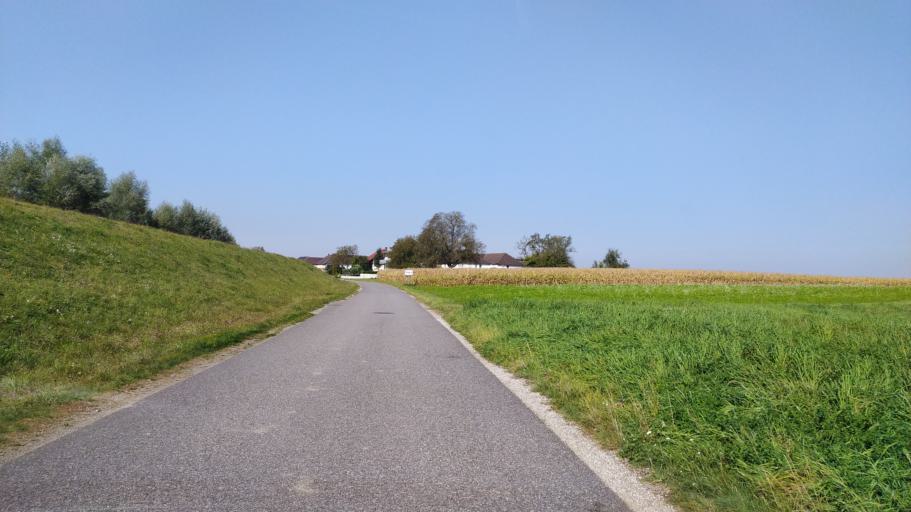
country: AT
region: Upper Austria
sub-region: Politischer Bezirk Perg
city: Perg
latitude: 48.1926
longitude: 14.7106
